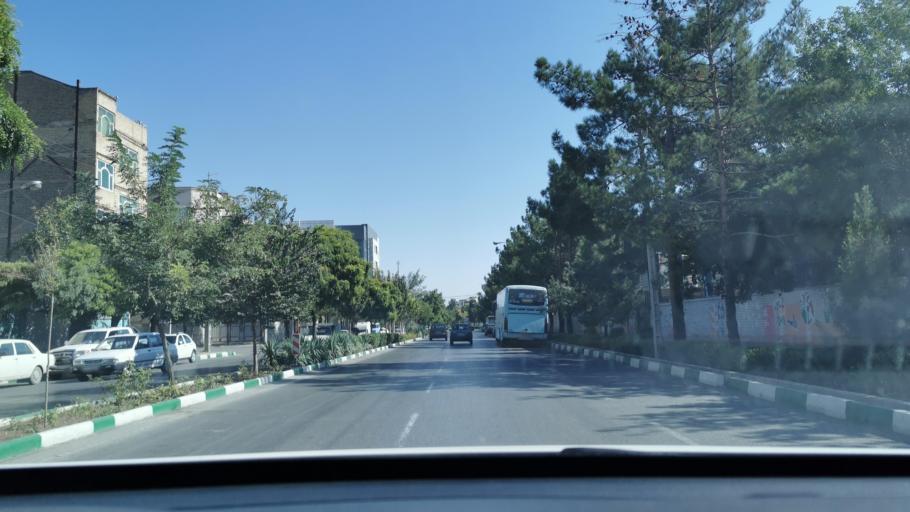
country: IR
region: Razavi Khorasan
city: Mashhad
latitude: 36.3342
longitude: 59.5925
